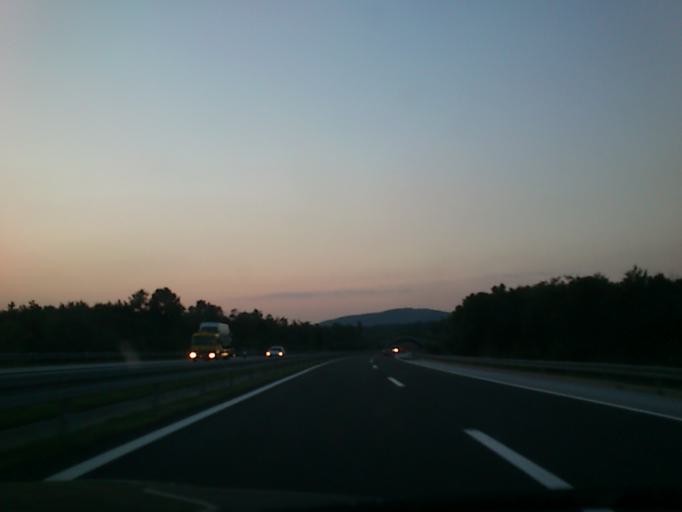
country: HR
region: Karlovacka
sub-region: Grad Ogulin
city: Ogulin
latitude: 45.3680
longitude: 15.2703
